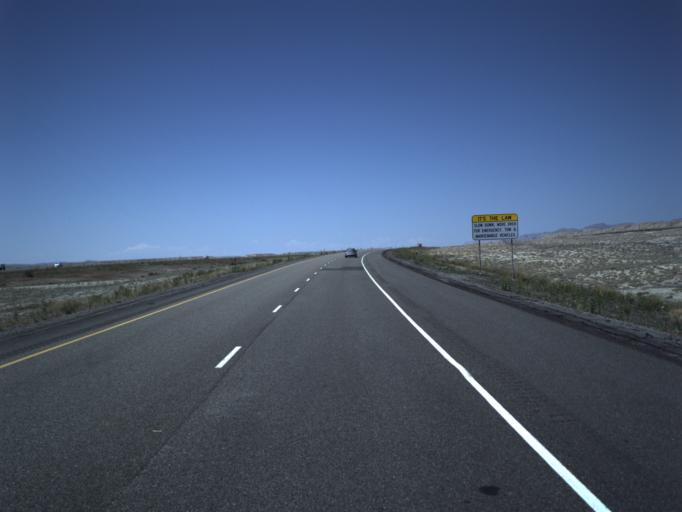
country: US
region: Utah
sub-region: Grand County
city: Moab
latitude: 38.9331
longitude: -109.4315
